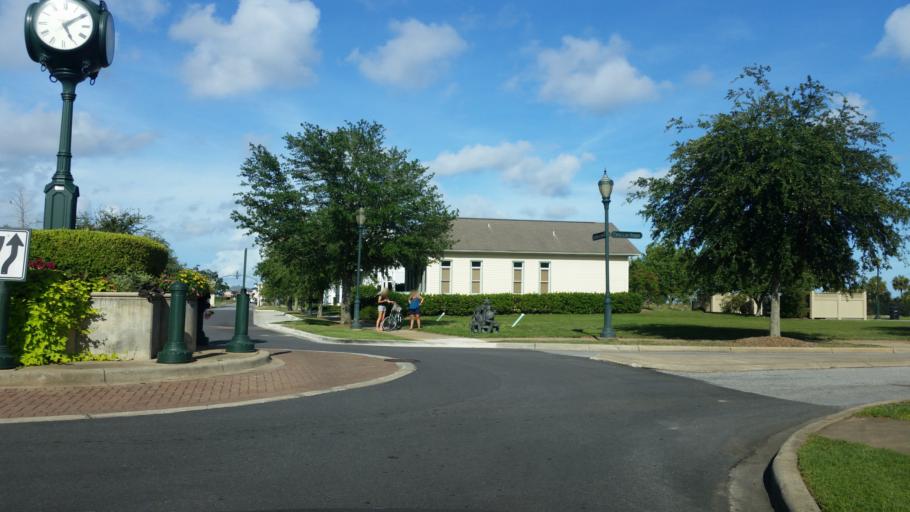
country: US
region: Florida
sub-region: Escambia County
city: Pensacola
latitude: 30.4128
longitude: -87.2066
